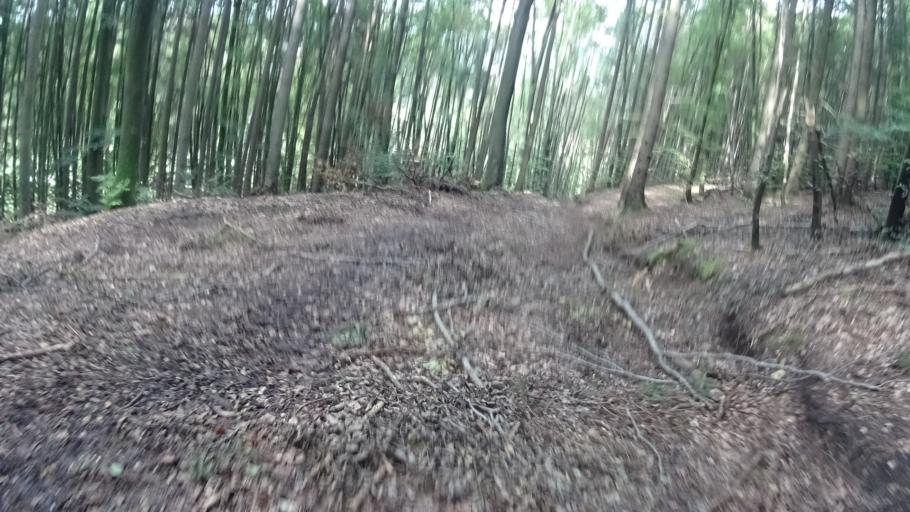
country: DE
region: Bavaria
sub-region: Upper Bavaria
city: Walting
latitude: 48.9025
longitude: 11.2978
